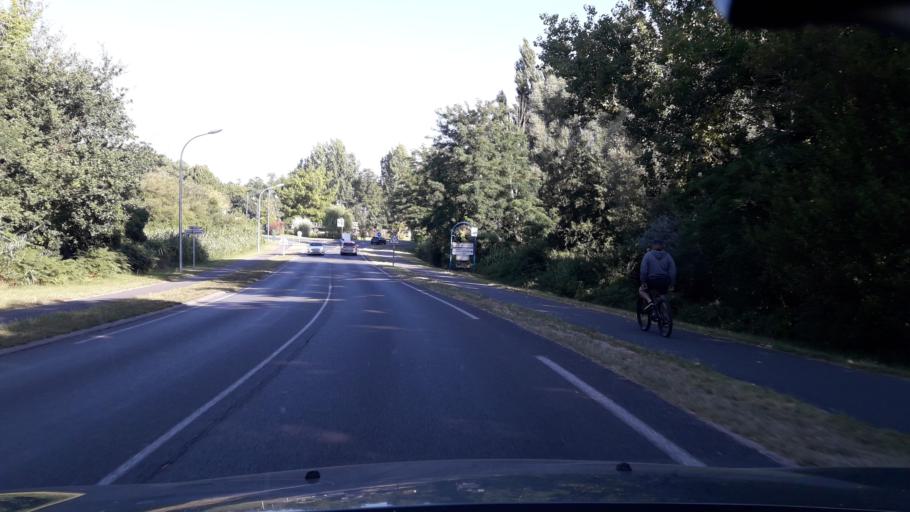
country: FR
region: Poitou-Charentes
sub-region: Departement de la Charente-Maritime
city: Les Mathes
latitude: 45.7112
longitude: -1.1594
